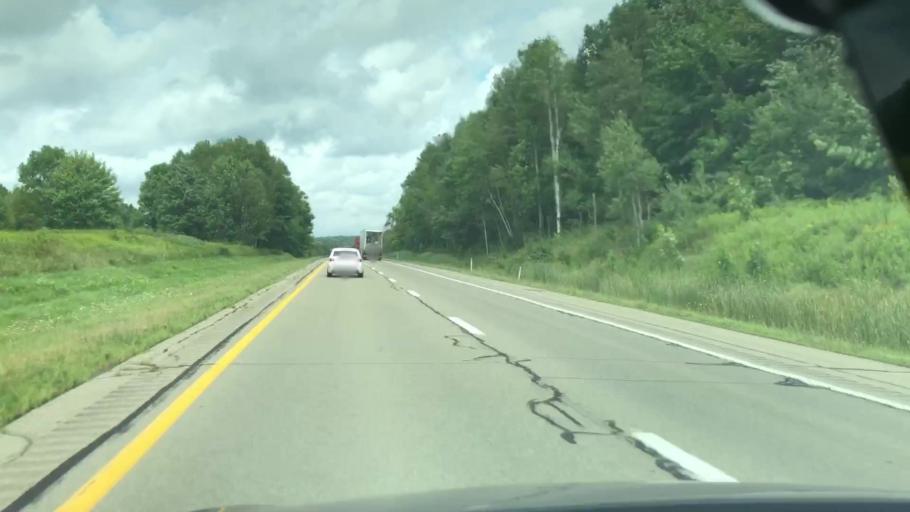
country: US
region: Pennsylvania
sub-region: Erie County
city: Edinboro
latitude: 41.7699
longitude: -80.1911
